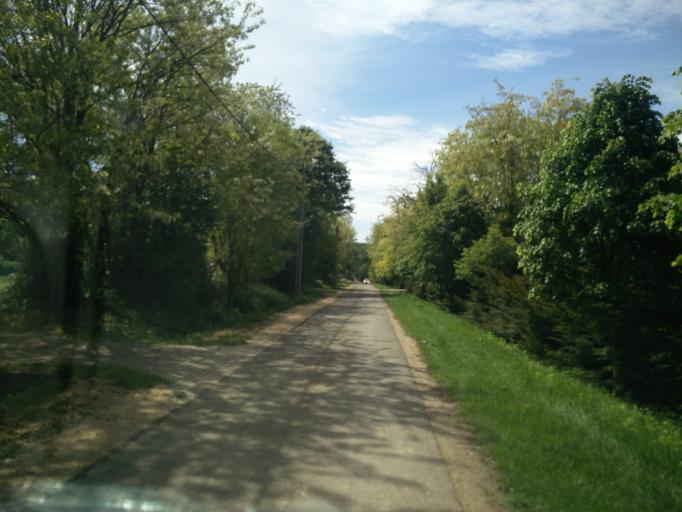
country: HU
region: Tolna
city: Szentgalpuszta
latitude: 46.2831
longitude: 18.6364
